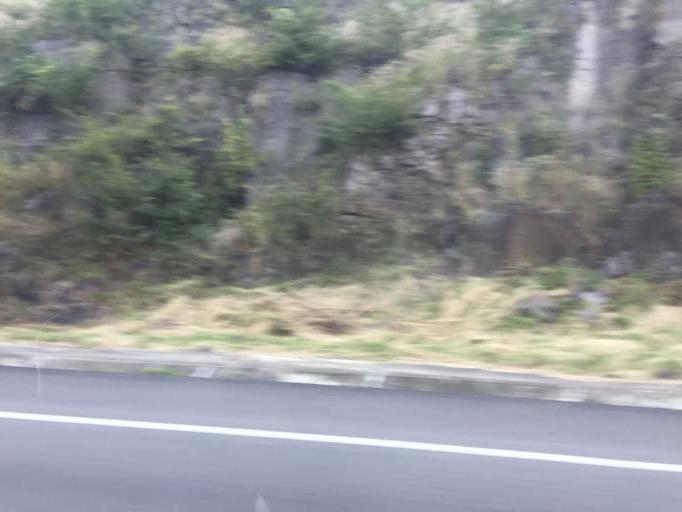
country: MX
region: Jalisco
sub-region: Zapotlanejo
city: La Mezquitera
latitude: 20.5339
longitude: -103.0148
